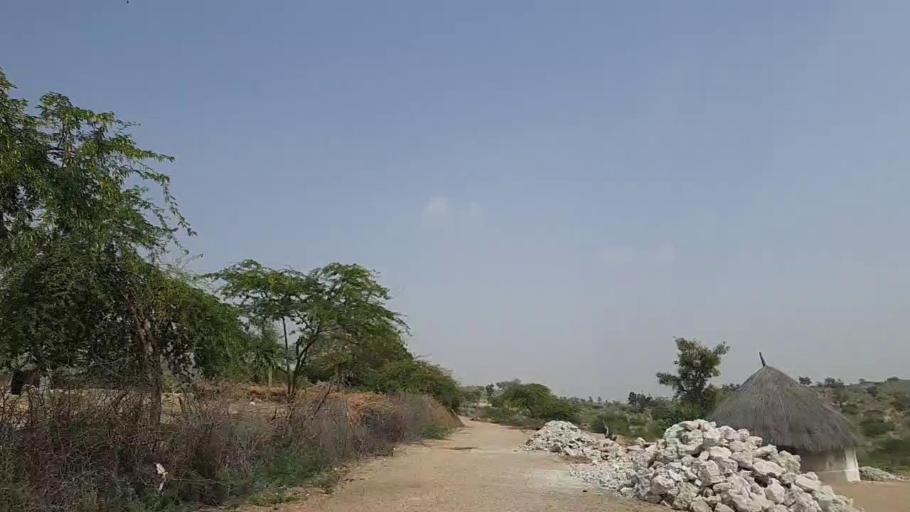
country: PK
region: Sindh
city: Mithi
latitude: 24.7631
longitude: 69.9318
